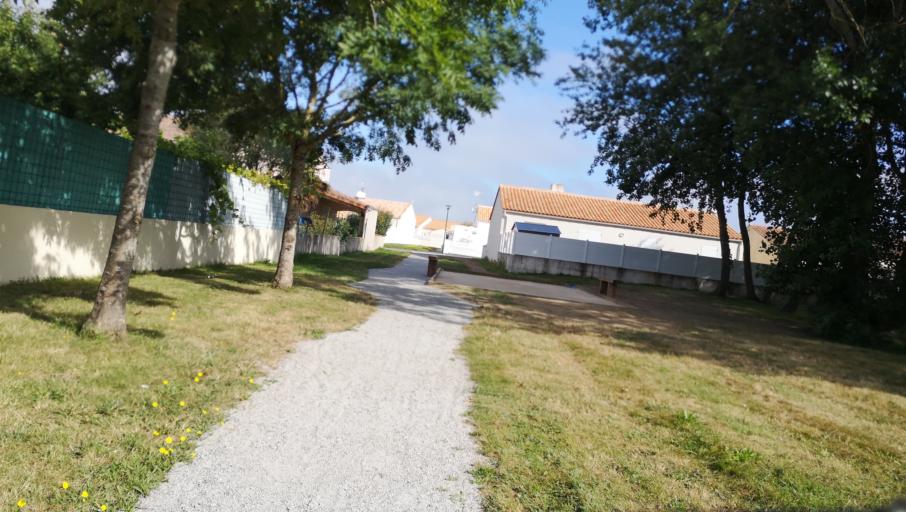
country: FR
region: Pays de la Loire
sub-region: Departement de la Vendee
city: Les Sables-d'Olonne
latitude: 46.5095
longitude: -1.7887
